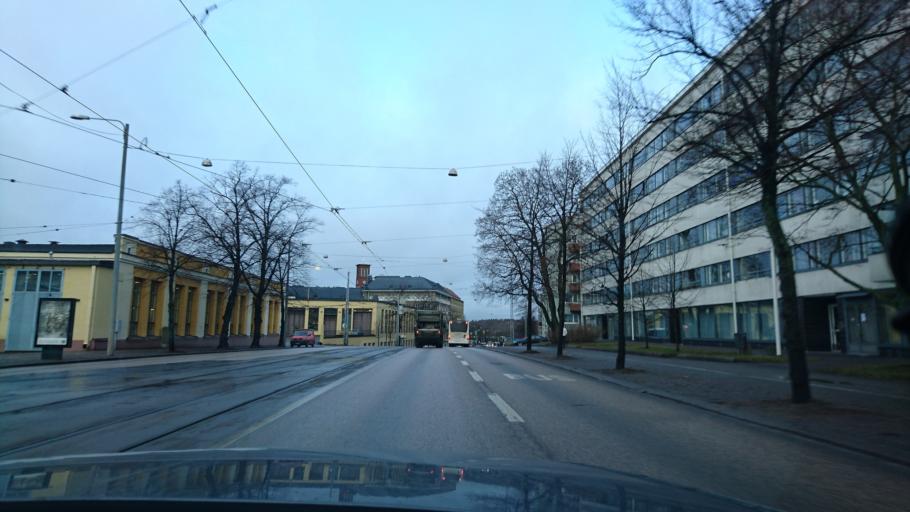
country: FI
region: Uusimaa
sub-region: Helsinki
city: Helsinki
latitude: 60.1944
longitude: 24.9638
